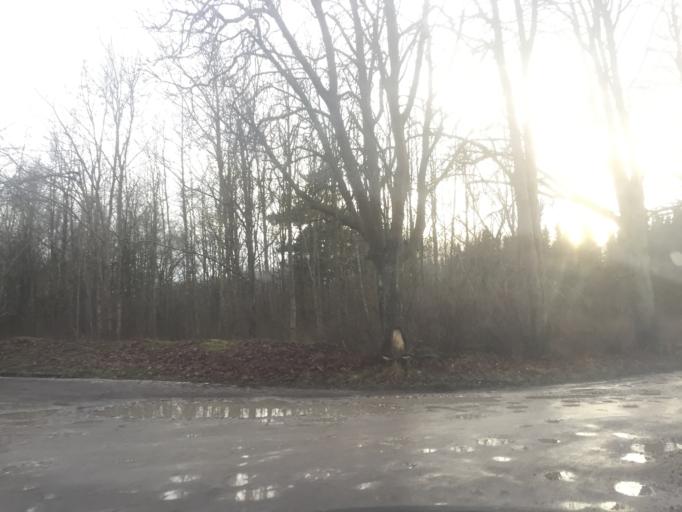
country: DK
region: Capital Region
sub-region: Albertslund Kommune
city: Albertslund
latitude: 55.6868
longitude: 12.3312
